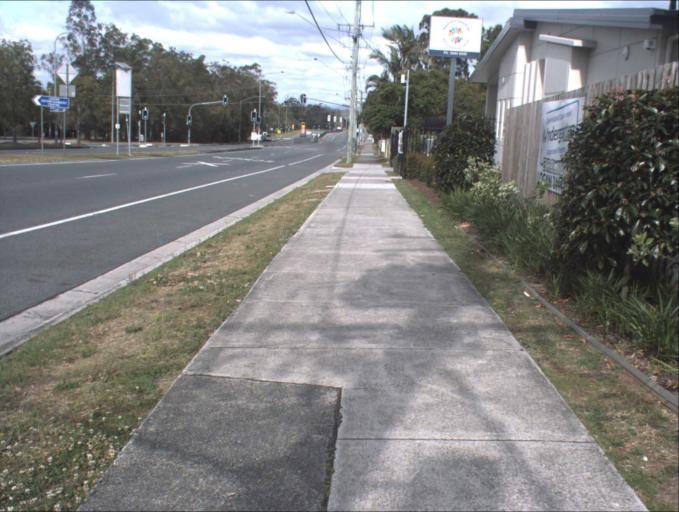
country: AU
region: Queensland
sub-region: Logan
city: Logan City
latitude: -27.6426
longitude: 153.1022
